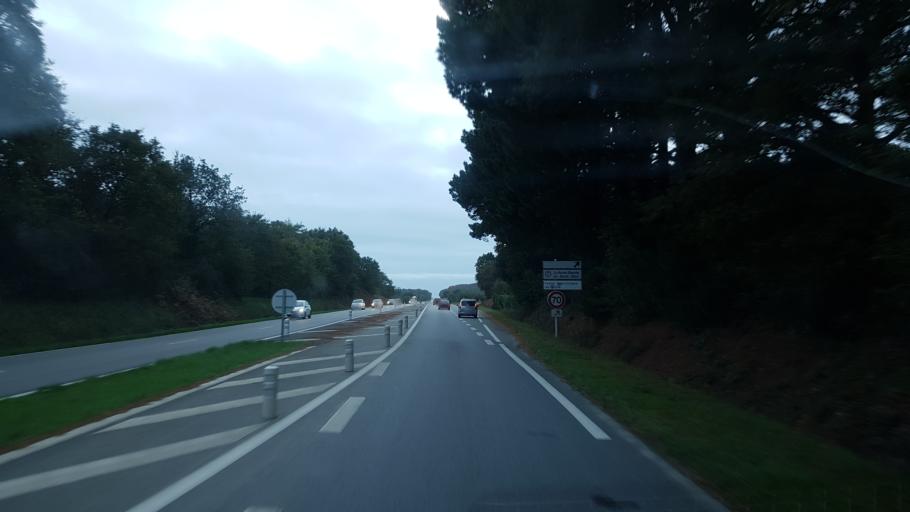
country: FR
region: Brittany
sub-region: Departement du Morbihan
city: Sarzeau
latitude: 47.5389
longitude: -2.7381
